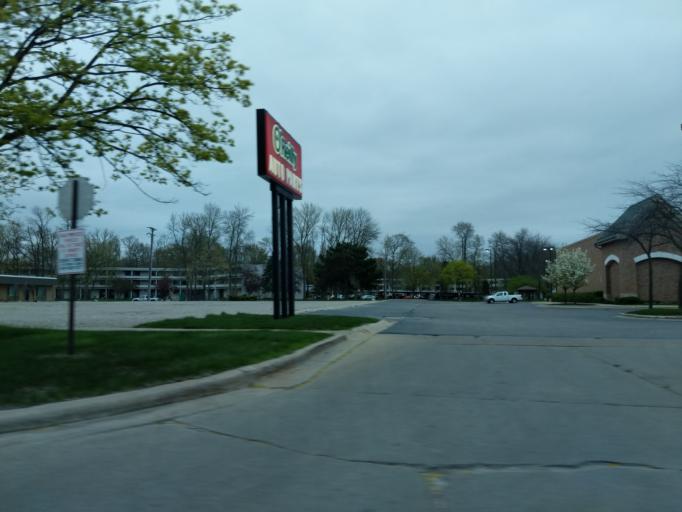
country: US
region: Michigan
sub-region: Midland County
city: Midland
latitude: 43.6210
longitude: -84.2211
